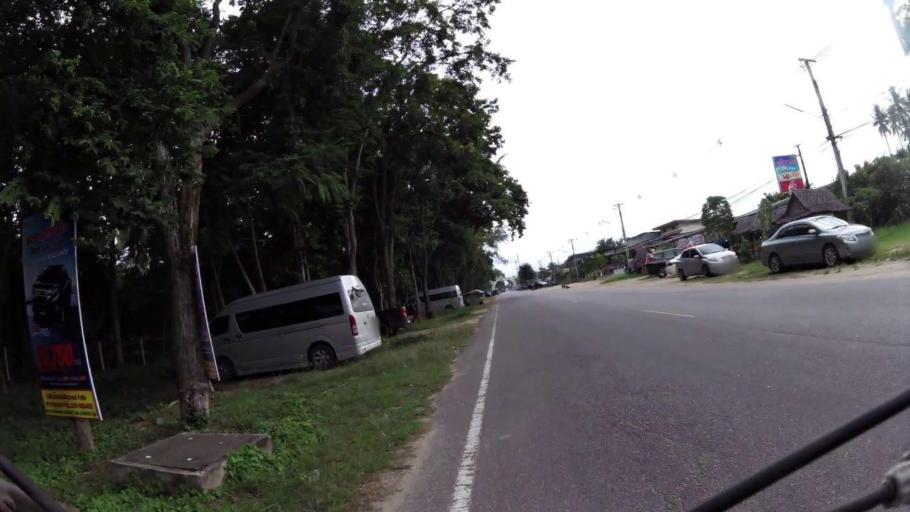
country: TH
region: Prachuap Khiri Khan
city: Prachuap Khiri Khan
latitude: 11.7551
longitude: 99.7920
